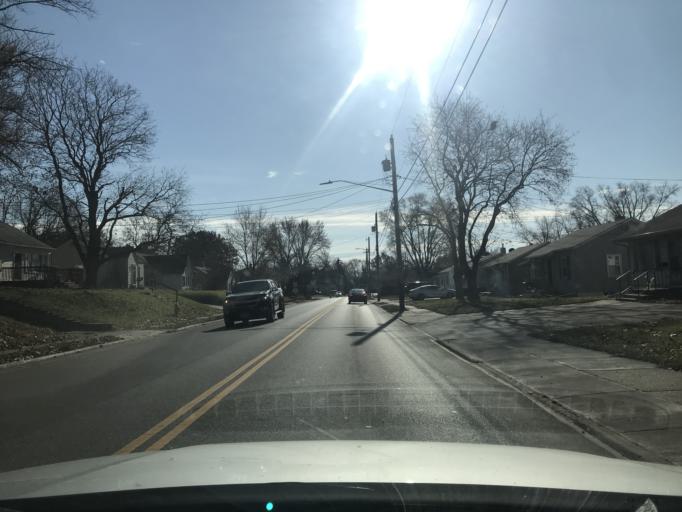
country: US
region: Iowa
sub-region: Scott County
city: Davenport
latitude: 41.5243
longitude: -90.6152
